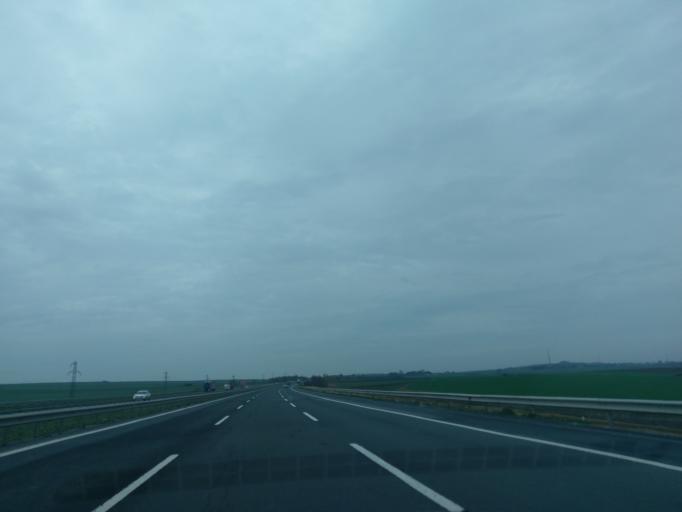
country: TR
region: Istanbul
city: Canta
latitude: 41.1278
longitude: 28.1623
